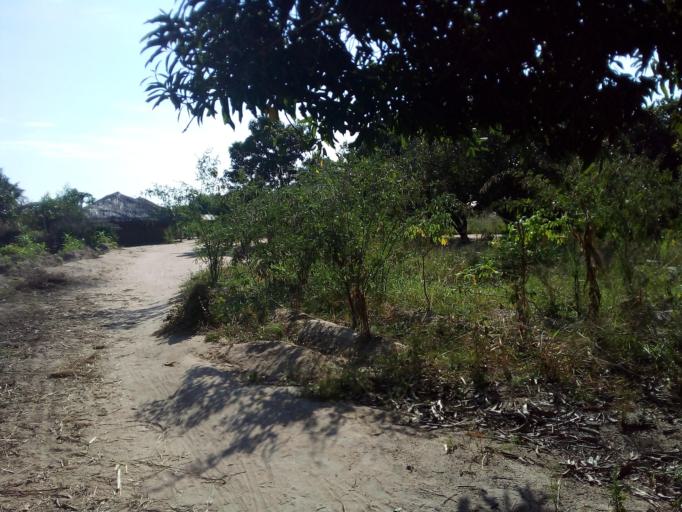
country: MZ
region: Zambezia
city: Quelimane
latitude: -17.5555
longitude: 36.7005
